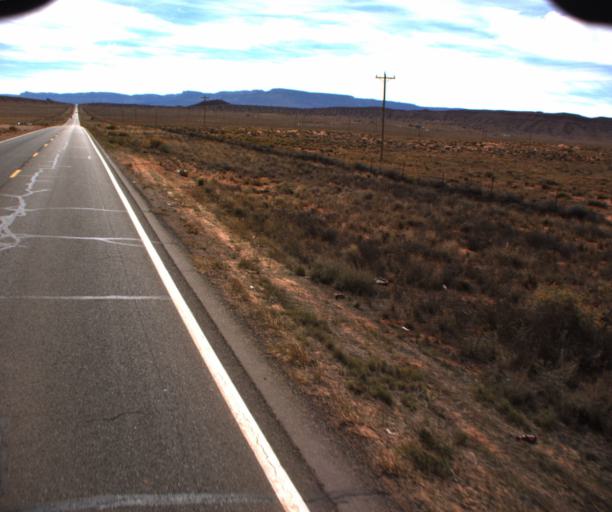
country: US
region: Arizona
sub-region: Navajo County
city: Kayenta
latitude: 36.7793
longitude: -110.2295
